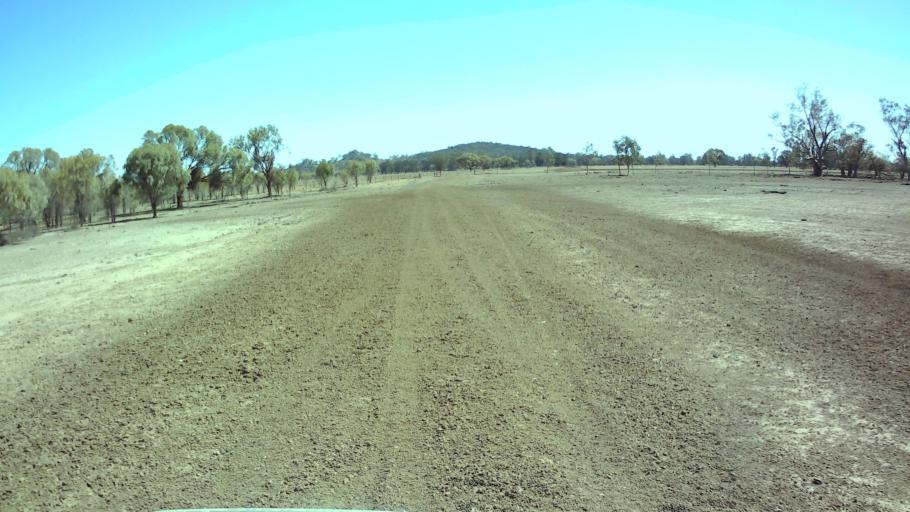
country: AU
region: New South Wales
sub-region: Bland
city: West Wyalong
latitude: -33.7512
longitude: 147.6598
